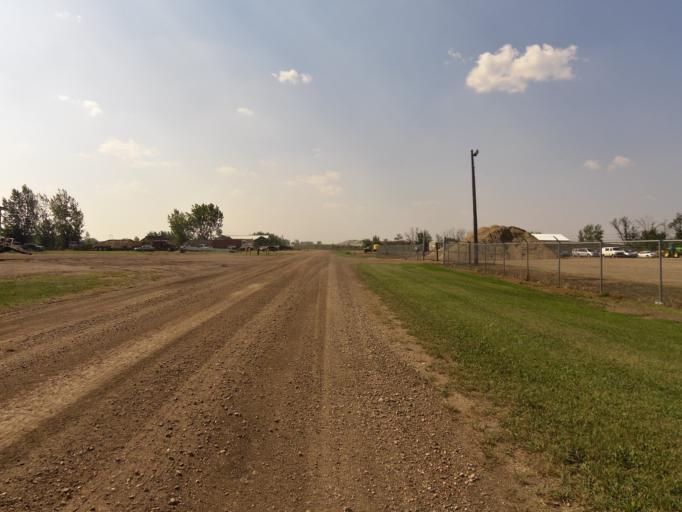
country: US
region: North Dakota
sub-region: Walsh County
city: Grafton
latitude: 48.4326
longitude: -97.4012
